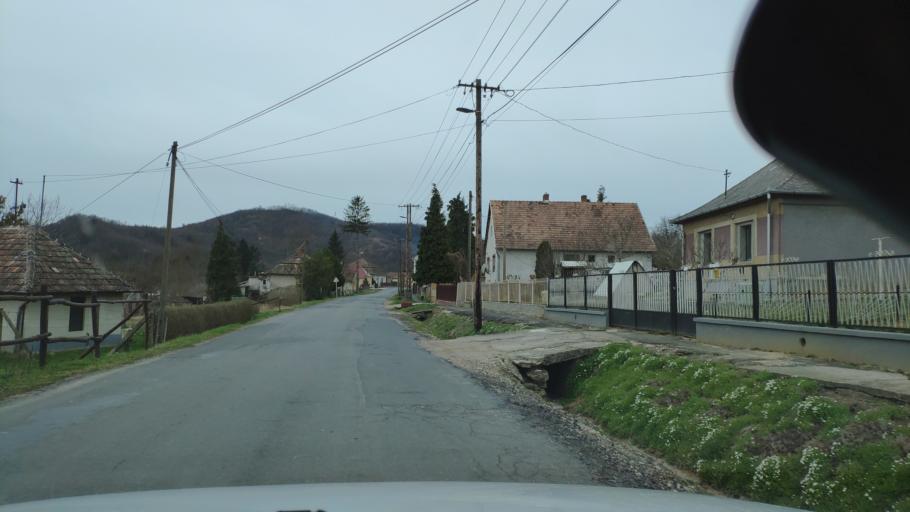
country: HU
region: Zala
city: Pacsa
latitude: 46.6743
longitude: 17.0803
